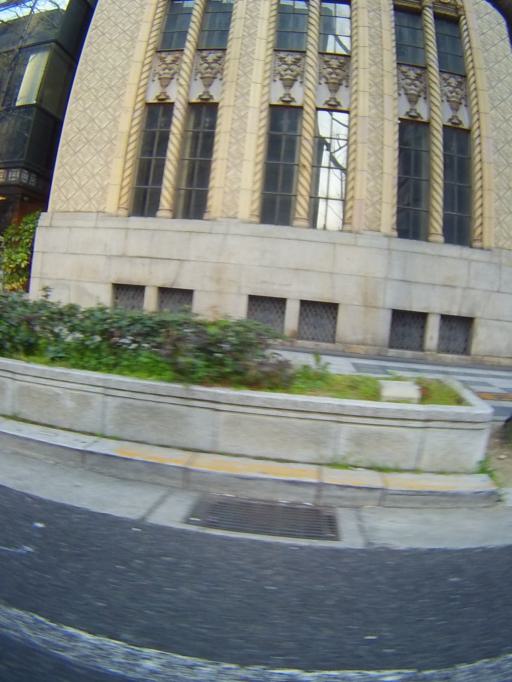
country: JP
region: Osaka
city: Osaka-shi
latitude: 34.6809
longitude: 135.5006
